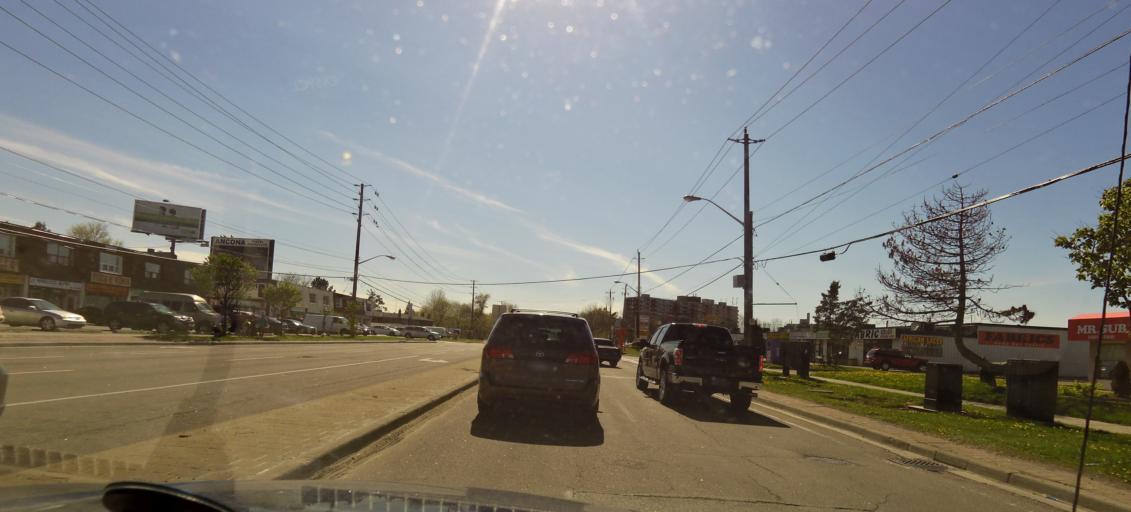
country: CA
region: Ontario
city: Concord
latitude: 43.7500
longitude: -79.5526
